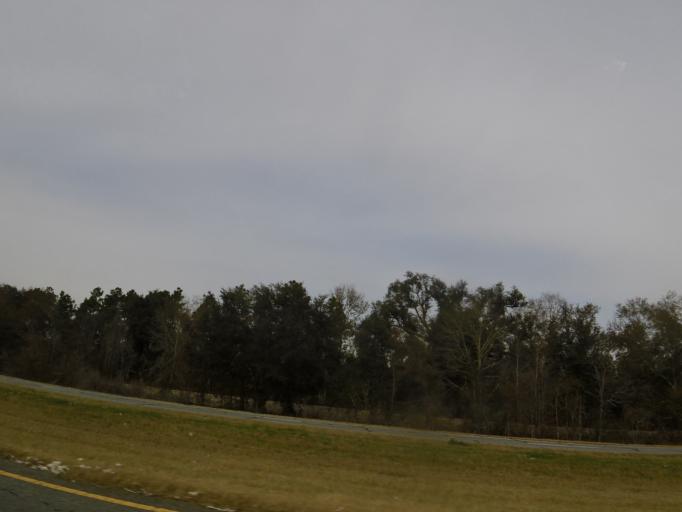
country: US
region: Georgia
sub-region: Seminole County
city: Donalsonville
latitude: 31.0232
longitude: -84.8363
